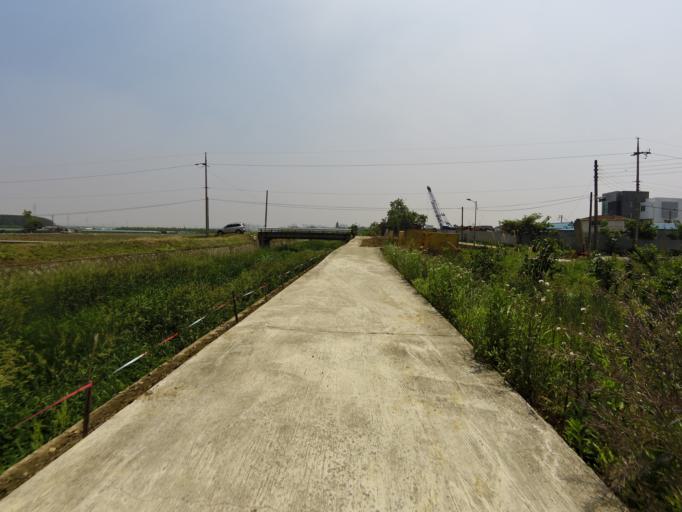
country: KR
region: Gyeongsangbuk-do
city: Gyeongsan-si
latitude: 35.8461
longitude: 128.7352
